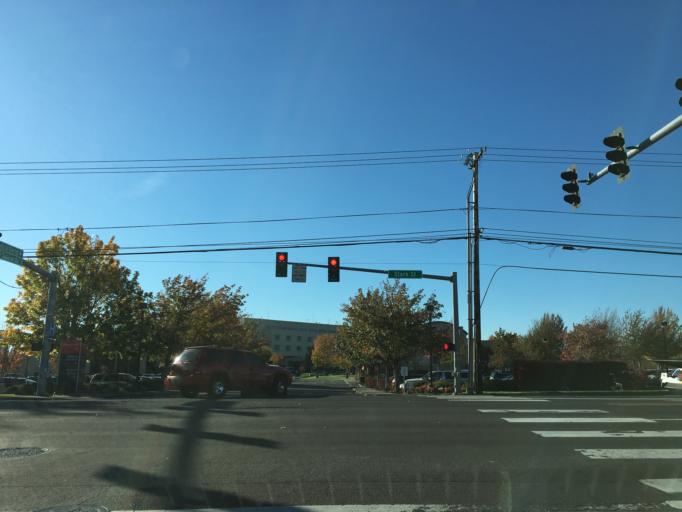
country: US
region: Oregon
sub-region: Multnomah County
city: Wood Village
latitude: 45.5192
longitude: -122.4071
